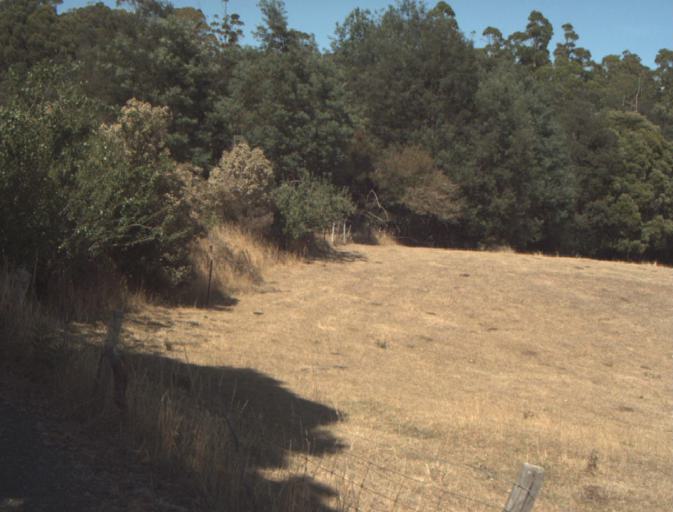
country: AU
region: Tasmania
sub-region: Launceston
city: Mayfield
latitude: -41.2552
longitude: 147.1861
